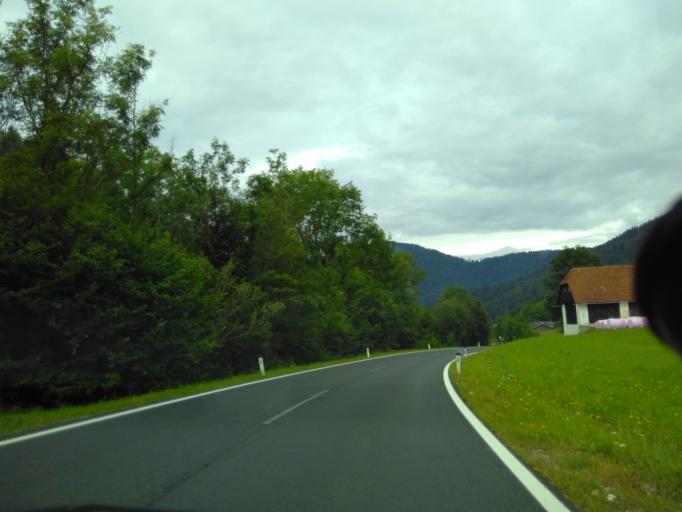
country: AT
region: Styria
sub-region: Politischer Bezirk Graz-Umgebung
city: Schrems bei Frohnleiten
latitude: 47.2745
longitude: 15.3849
